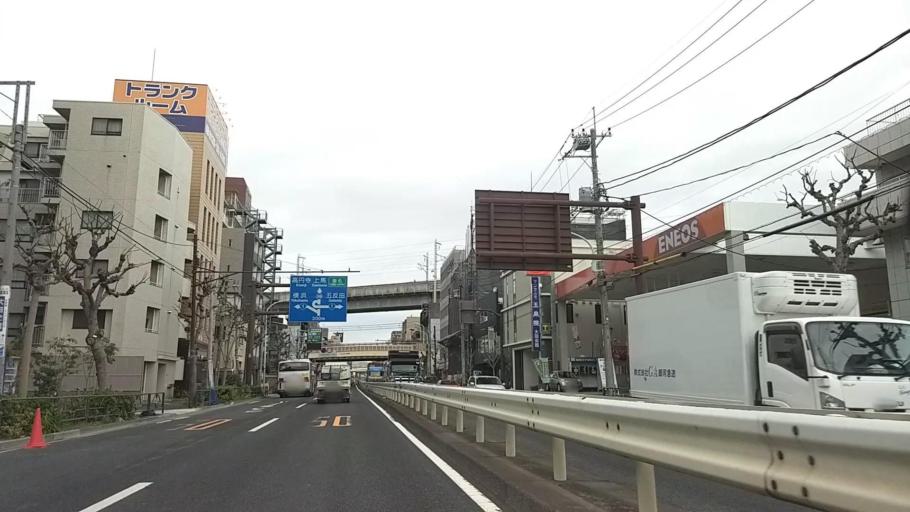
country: JP
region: Kanagawa
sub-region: Kawasaki-shi
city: Kawasaki
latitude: 35.5933
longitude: 139.7157
